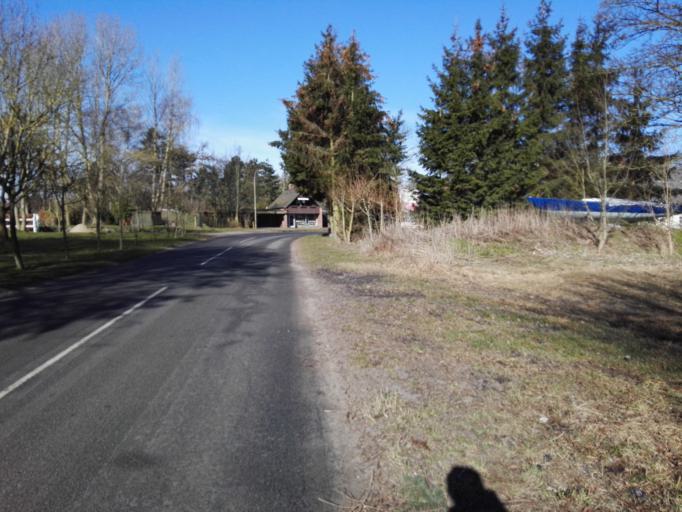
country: DK
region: Zealand
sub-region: Lejre Kommune
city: Ejby
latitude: 55.7658
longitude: 11.8175
